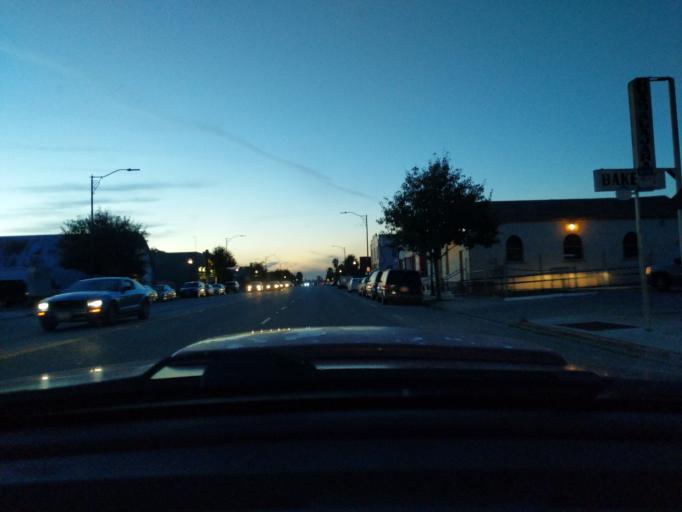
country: US
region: California
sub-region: Monterey County
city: Salinas
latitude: 36.6766
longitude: -121.6318
